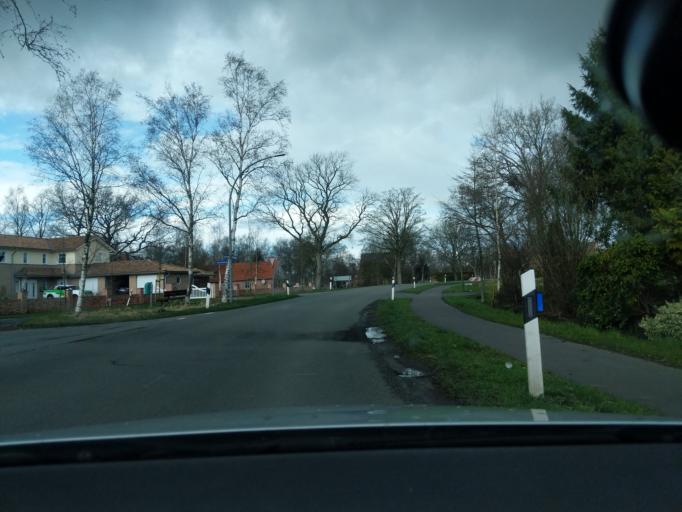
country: DE
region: Lower Saxony
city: Drochtersen
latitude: 53.6540
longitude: 9.4255
